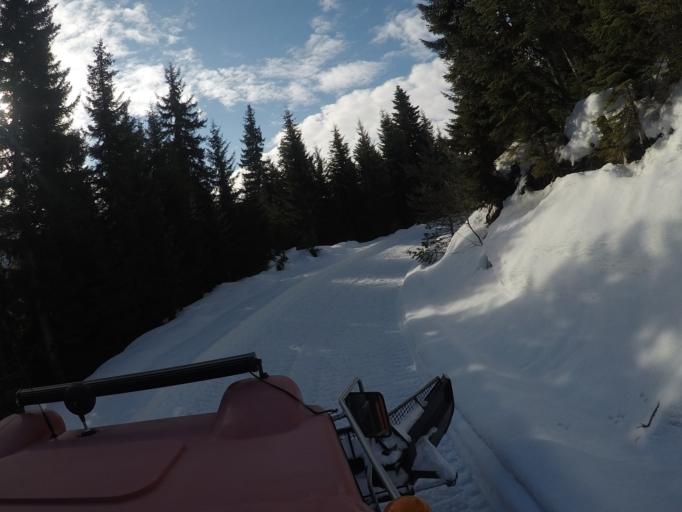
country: GE
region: Samtskhe-Javakheti
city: Adigeni
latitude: 41.6467
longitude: 42.5994
